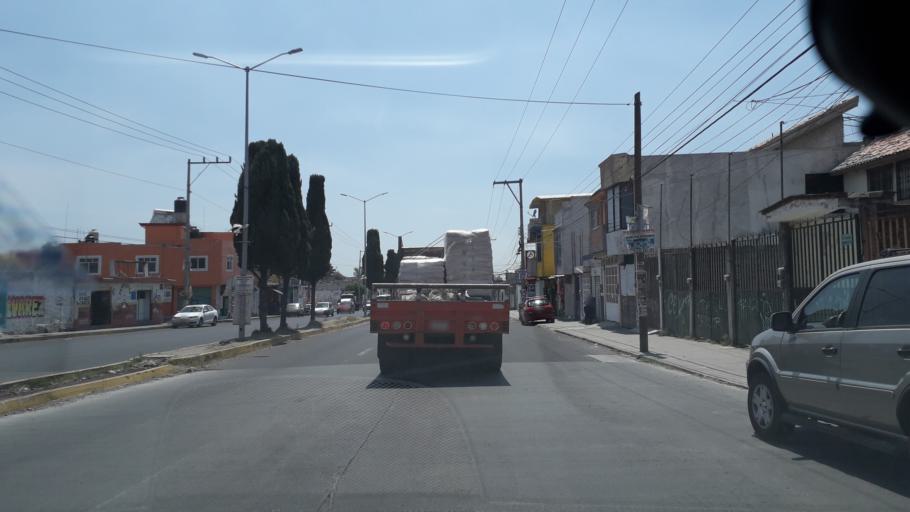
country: MX
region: Puebla
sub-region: Amozoc
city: Casa Blanca
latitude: 19.0663
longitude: -98.1203
